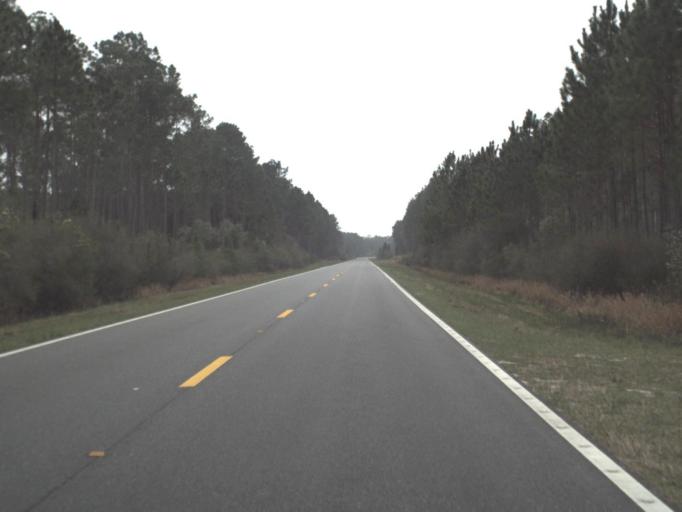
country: US
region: Florida
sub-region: Liberty County
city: Bristol
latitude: 30.3045
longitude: -84.8311
